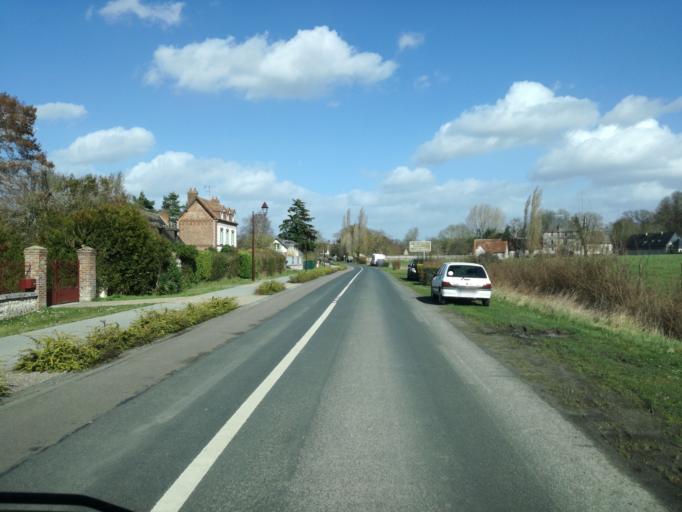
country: FR
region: Haute-Normandie
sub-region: Departement de la Seine-Maritime
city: Sahurs
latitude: 49.3559
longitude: 0.9413
